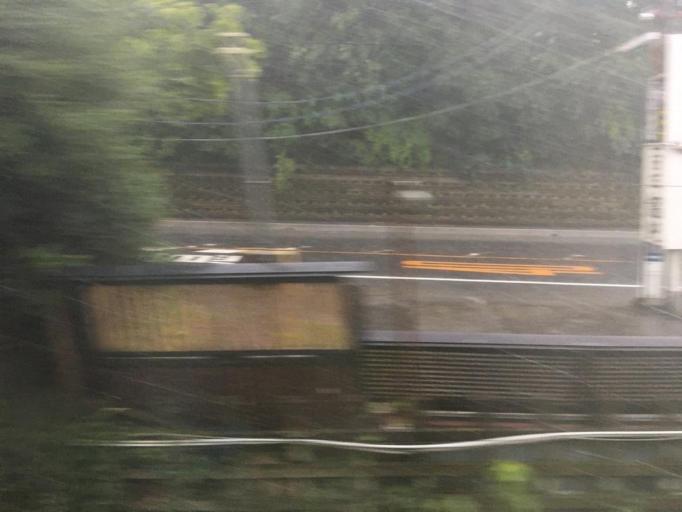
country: JP
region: Gunma
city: Tatebayashi
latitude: 36.2649
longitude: 139.5127
